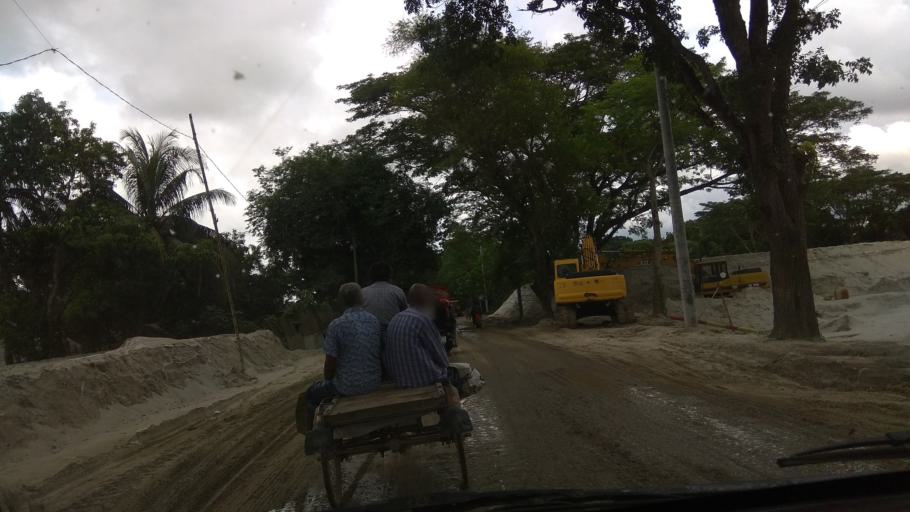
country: BD
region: Khulna
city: Kalia
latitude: 23.1970
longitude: 89.6966
